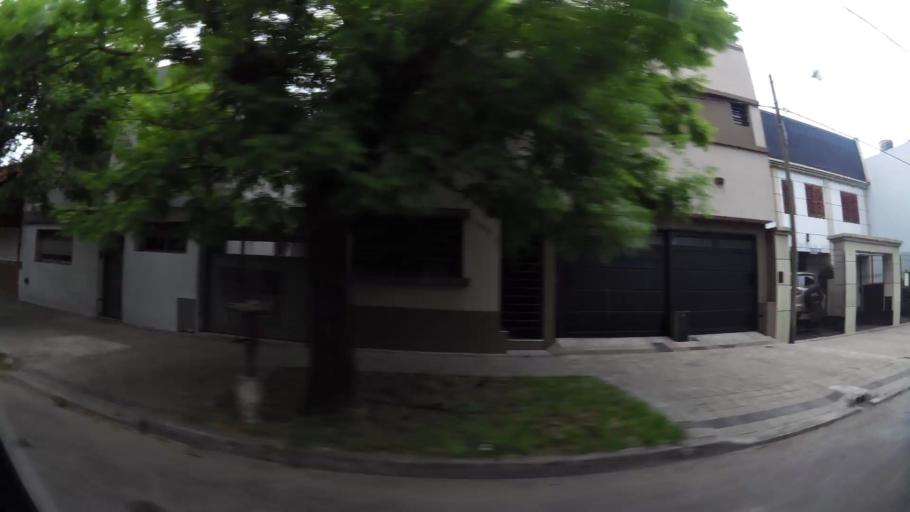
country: AR
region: Buenos Aires
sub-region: Partido de La Plata
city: La Plata
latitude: -34.9250
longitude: -57.9855
